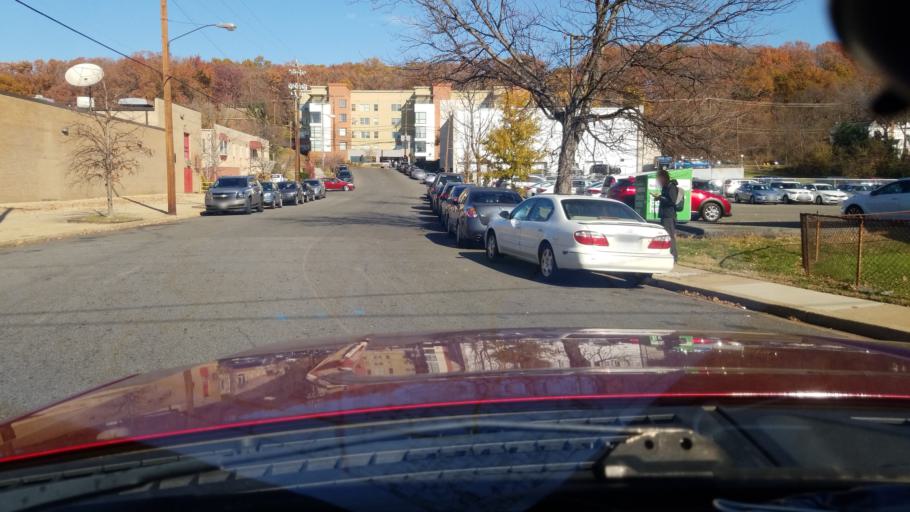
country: US
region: Maryland
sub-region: Prince George's County
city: Capitol Heights
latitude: 38.8929
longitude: -76.9473
